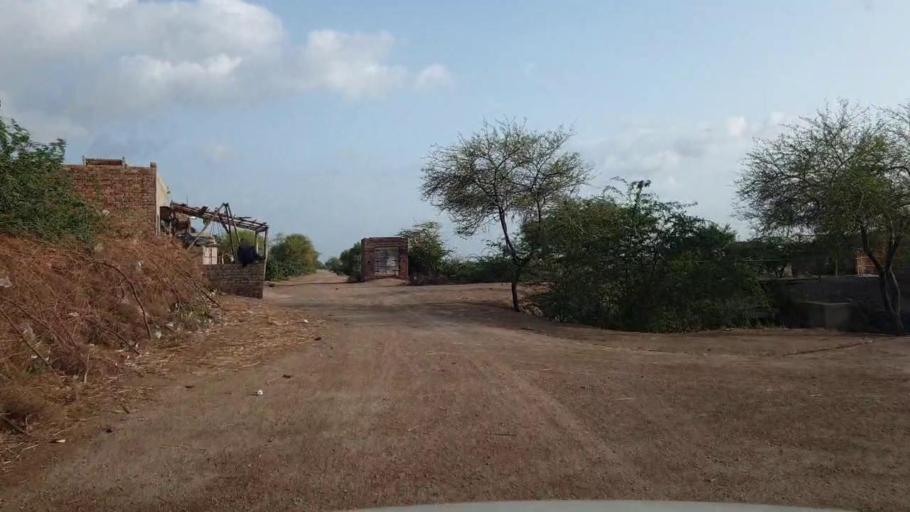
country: PK
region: Sindh
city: Kario
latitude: 24.8075
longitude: 68.6471
